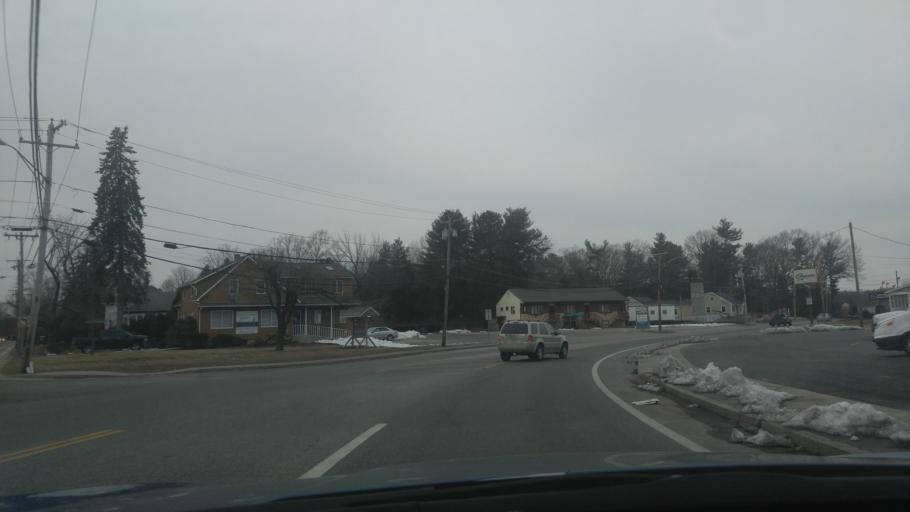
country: US
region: Rhode Island
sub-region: Kent County
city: West Warwick
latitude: 41.6836
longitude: -71.5604
